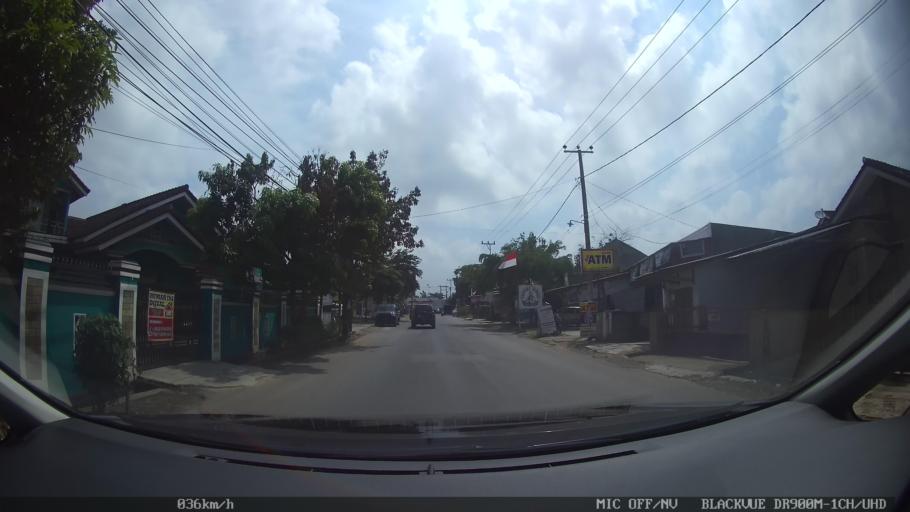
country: ID
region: Lampung
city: Kedaton
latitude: -5.3472
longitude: 105.2951
